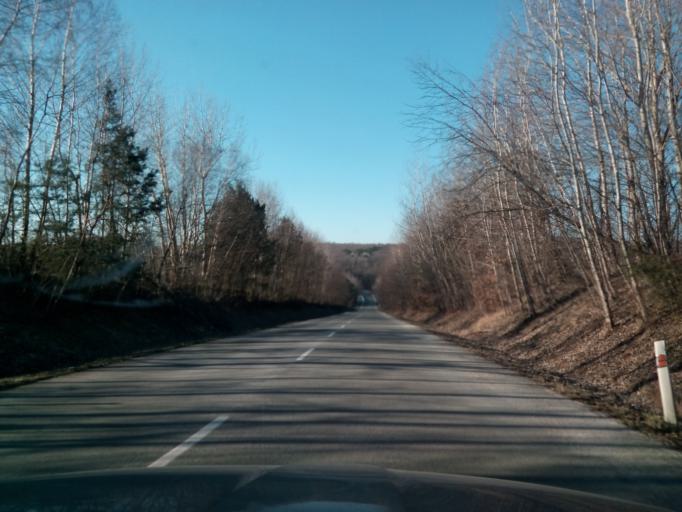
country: SK
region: Kosicky
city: Moldava nad Bodvou
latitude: 48.6912
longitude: 21.0501
